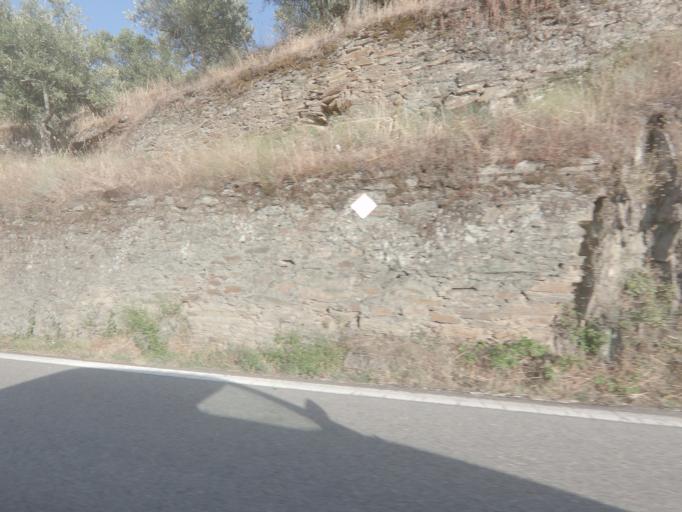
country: PT
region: Viseu
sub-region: Tabuaco
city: Tabuaco
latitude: 41.1717
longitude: -7.5552
